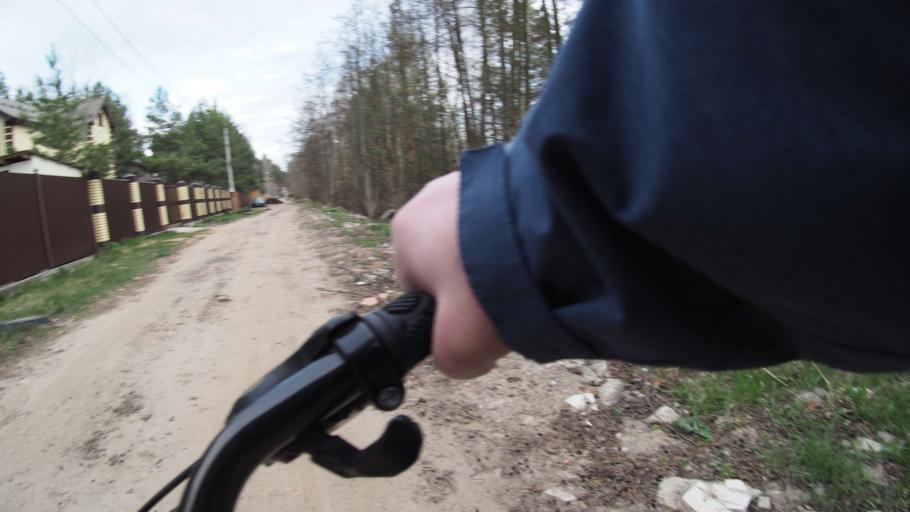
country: RU
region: Moskovskaya
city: Ramenskoye
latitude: 55.5896
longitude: 38.2925
